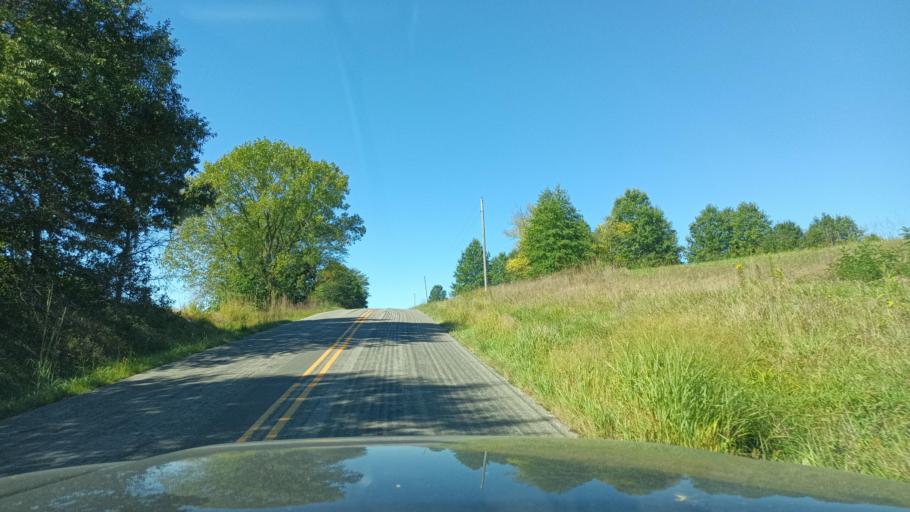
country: US
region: Missouri
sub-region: Scotland County
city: Memphis
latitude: 40.3543
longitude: -92.2802
